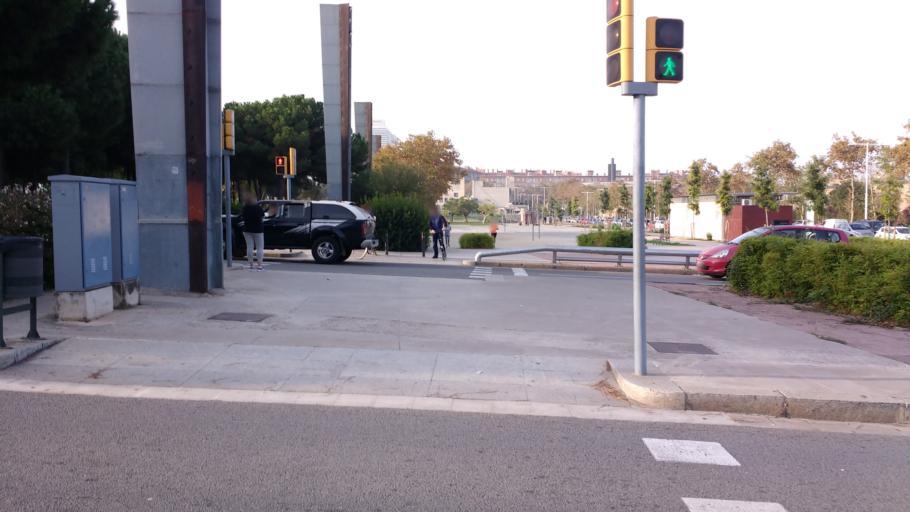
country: ES
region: Catalonia
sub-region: Provincia de Barcelona
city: Sant Marti
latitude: 41.3962
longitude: 2.2056
